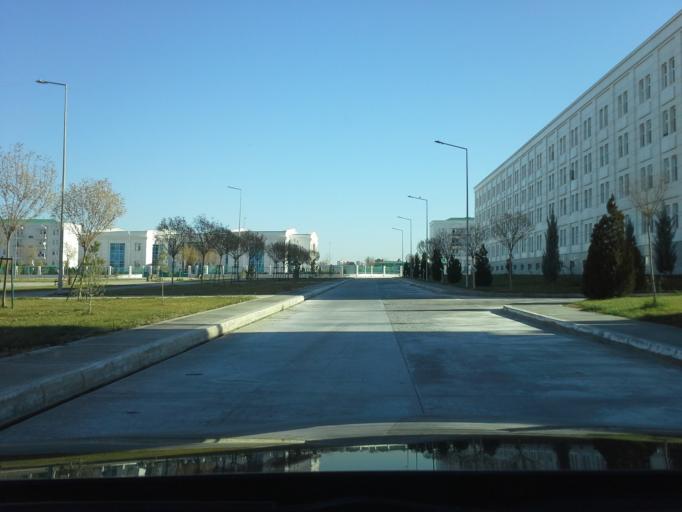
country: TM
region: Ahal
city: Ashgabat
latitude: 37.9706
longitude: 58.3358
